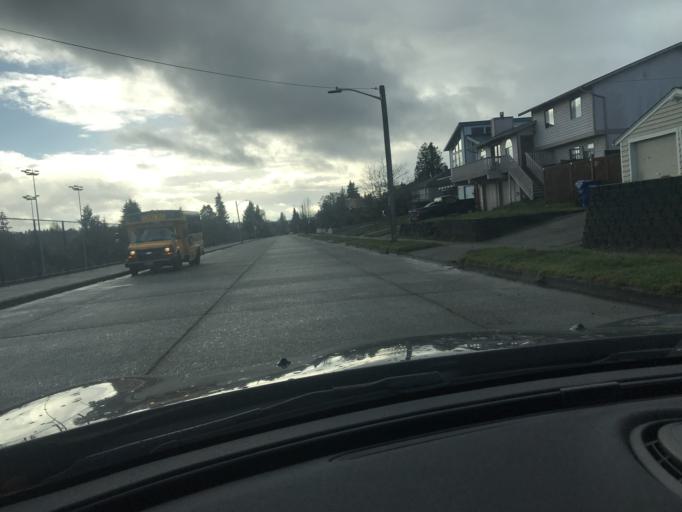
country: US
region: Washington
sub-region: King County
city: White Center
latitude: 47.5263
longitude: -122.3699
